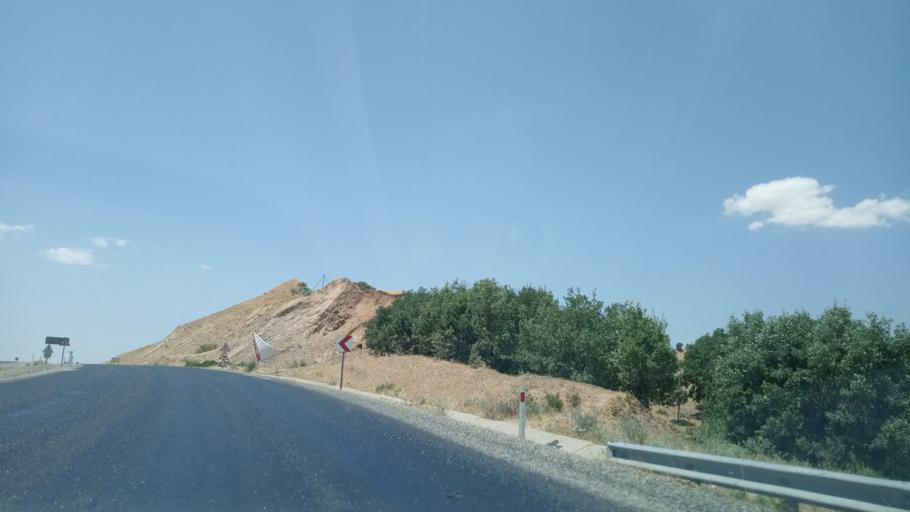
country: TR
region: Batman
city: Kozluk
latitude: 38.1736
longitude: 41.4463
